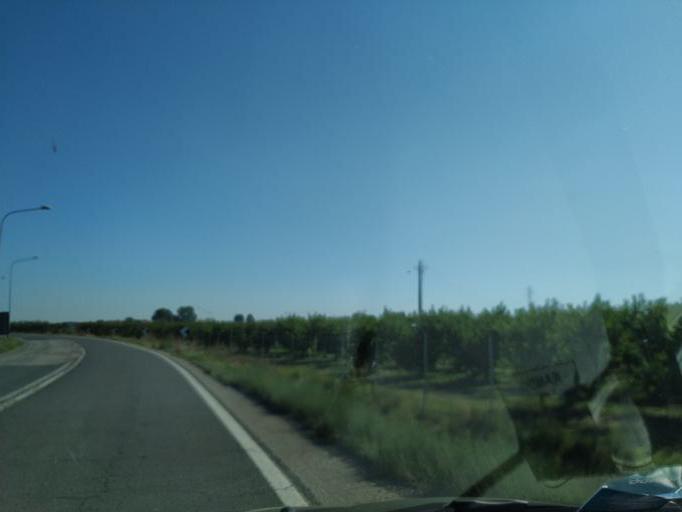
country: IT
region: Emilia-Romagna
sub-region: Provincia di Bologna
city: Decima
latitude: 44.6987
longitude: 11.2347
